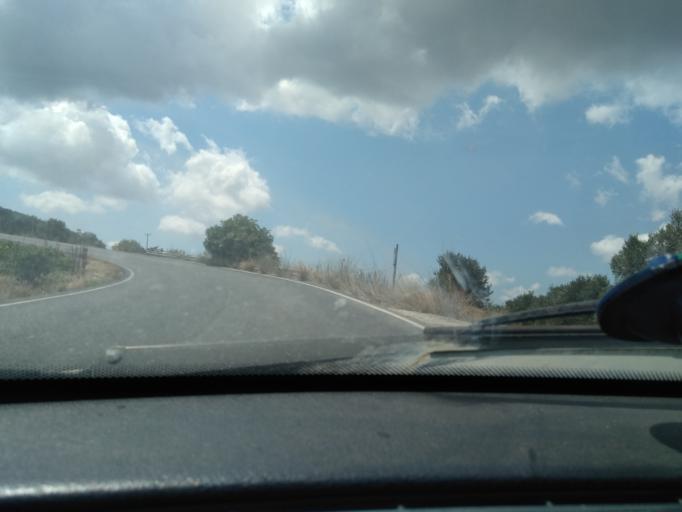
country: GR
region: Crete
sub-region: Nomos Lasithiou
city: Siteia
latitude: 35.1097
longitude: 26.0572
